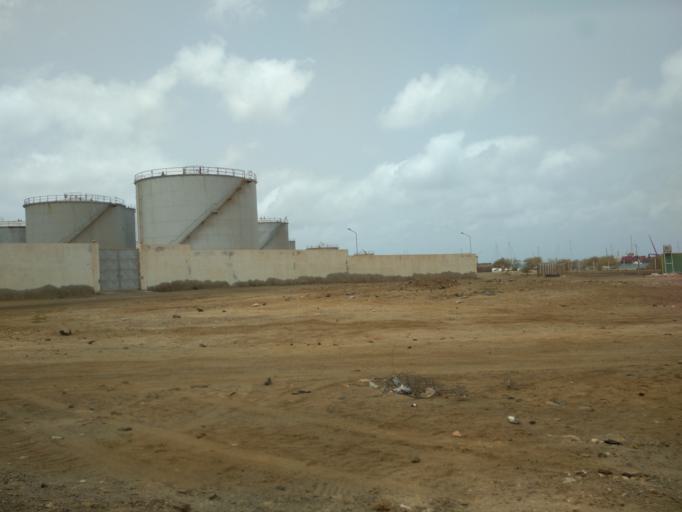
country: CV
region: Sal
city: Espargos
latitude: 16.7579
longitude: -22.9778
